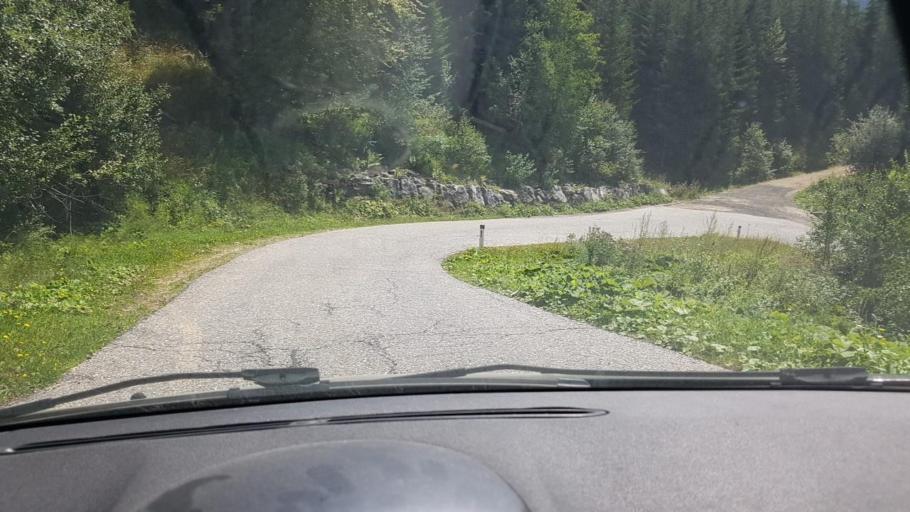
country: SI
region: Jezersko
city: Zgornje Jezersko
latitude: 46.4177
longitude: 14.5735
